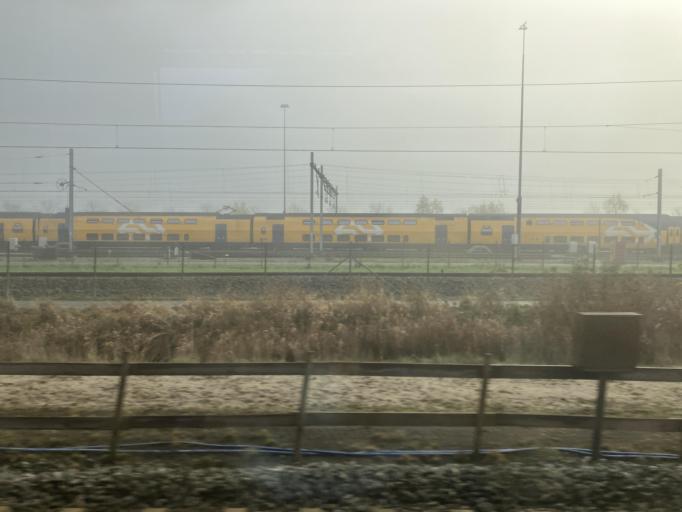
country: NL
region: North Holland
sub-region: Gemeente Haarlemmermeer
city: Hoofddorp
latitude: 52.2837
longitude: 4.6809
